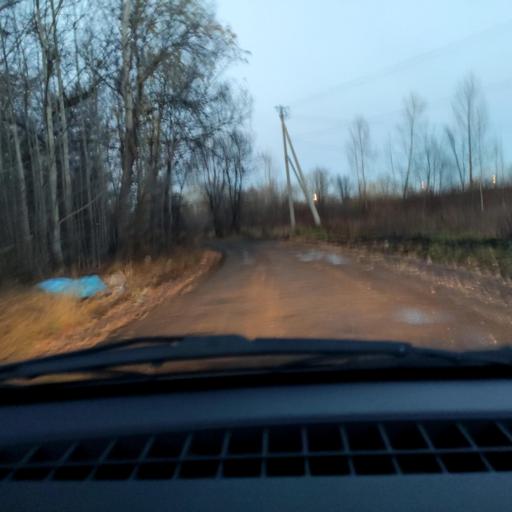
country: RU
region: Bashkortostan
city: Ufa
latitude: 54.6564
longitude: 55.8874
